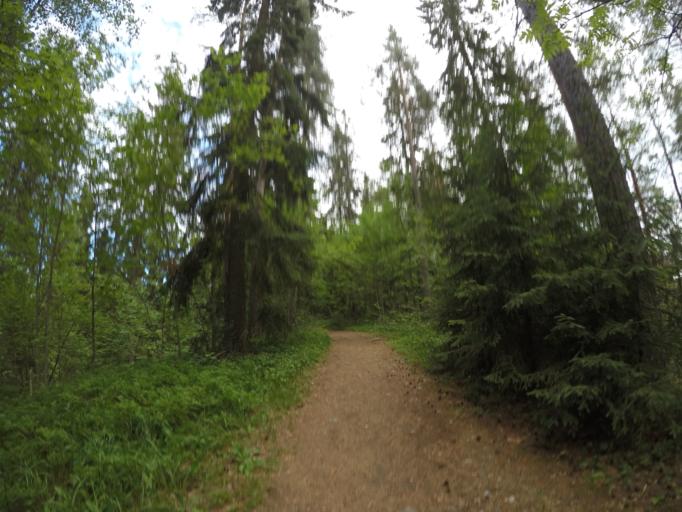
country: FI
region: Haeme
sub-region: Haemeenlinna
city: Parola
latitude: 61.0068
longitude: 24.3959
